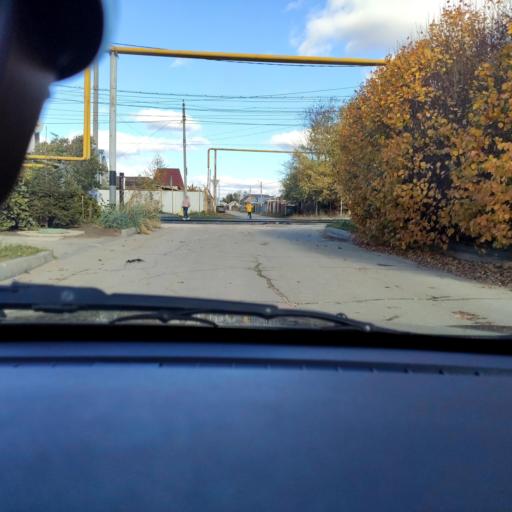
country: RU
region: Samara
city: Podstepki
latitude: 53.5120
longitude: 49.2314
